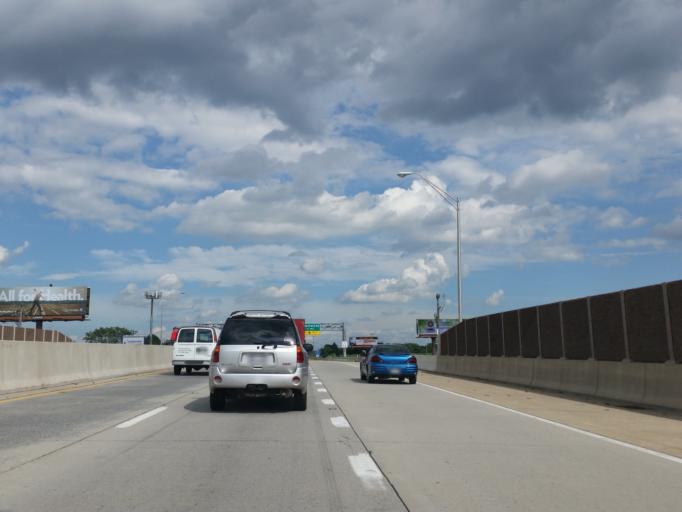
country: US
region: Pennsylvania
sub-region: Lancaster County
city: Lancaster
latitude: 40.0529
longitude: -76.2630
